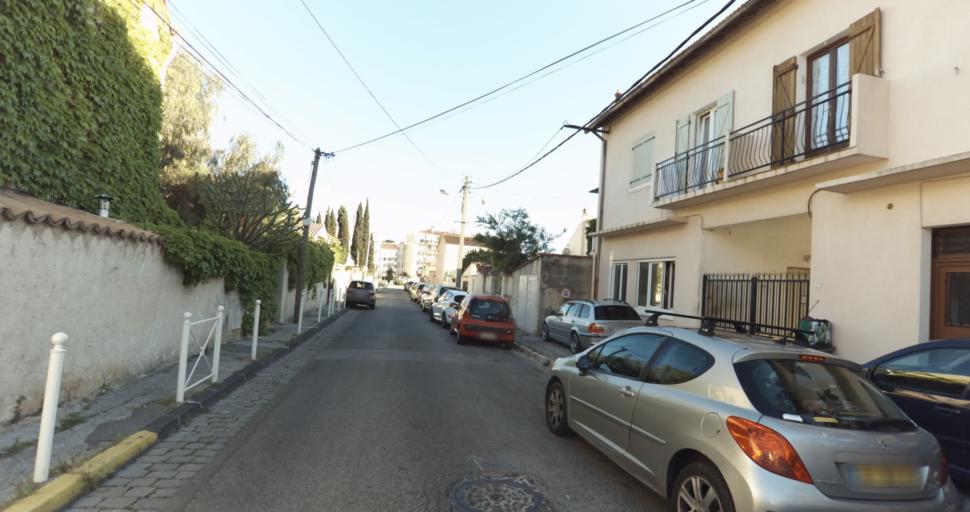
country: FR
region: Provence-Alpes-Cote d'Azur
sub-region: Departement du Var
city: La Seyne-sur-Mer
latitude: 43.1285
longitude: 5.8995
